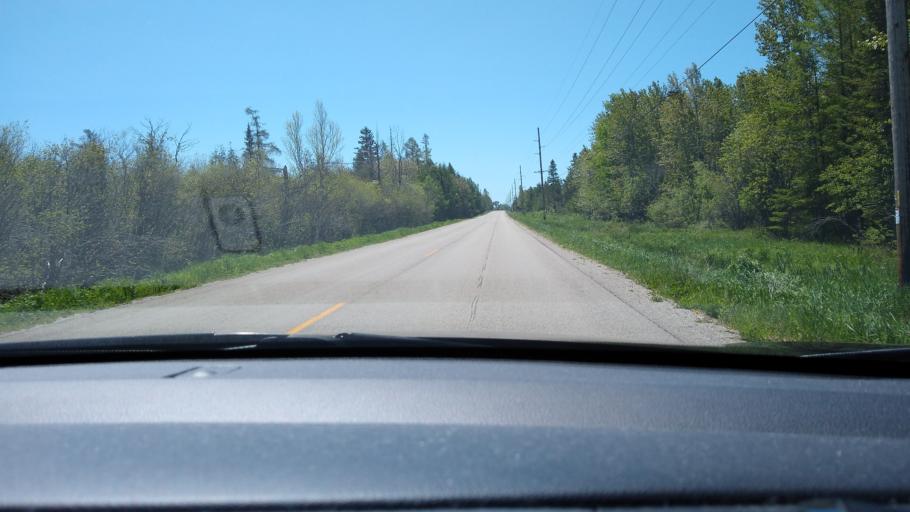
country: US
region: Michigan
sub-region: Delta County
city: Escanaba
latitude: 45.8546
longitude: -87.1841
